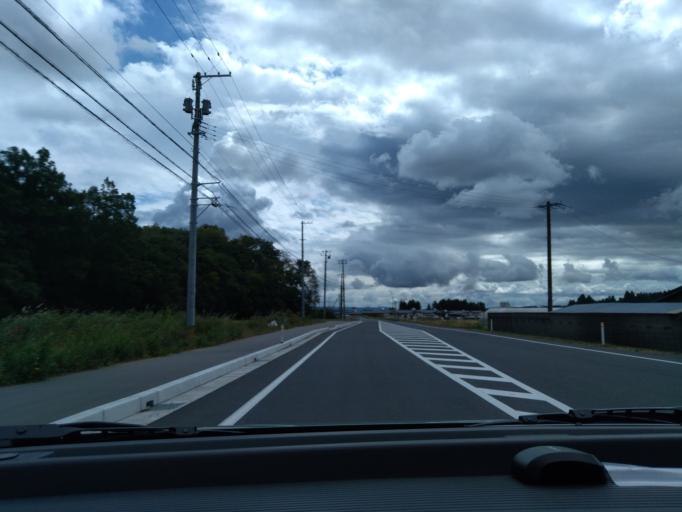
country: JP
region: Iwate
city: Ichinoseki
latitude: 38.8584
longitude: 141.1621
